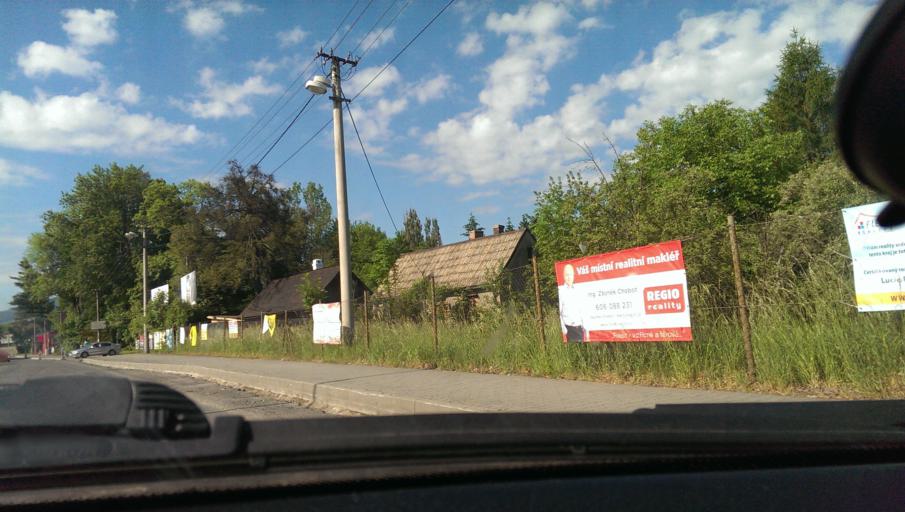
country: CZ
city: Frydlant nad Ostravici
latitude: 49.5840
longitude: 18.3590
